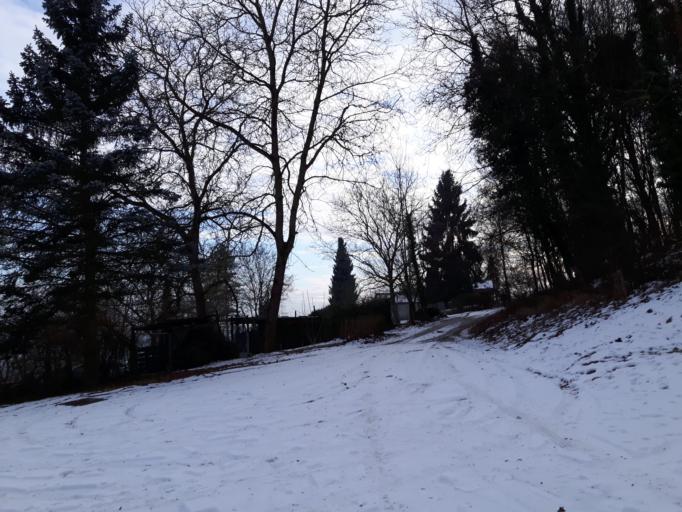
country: DE
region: Baden-Wuerttemberg
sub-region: Regierungsbezirk Stuttgart
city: Besigheim
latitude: 49.0074
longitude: 9.1369
